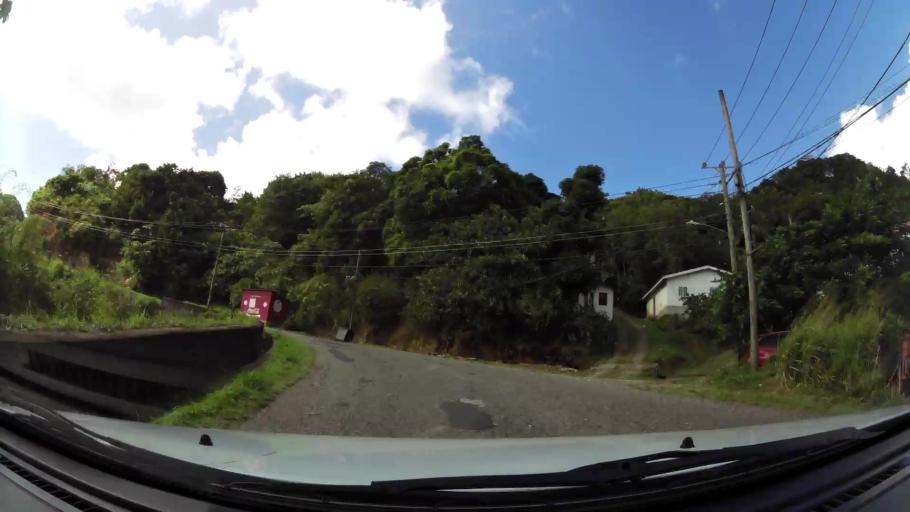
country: LC
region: Castries Quarter
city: Castries
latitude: 13.9910
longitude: -60.9963
